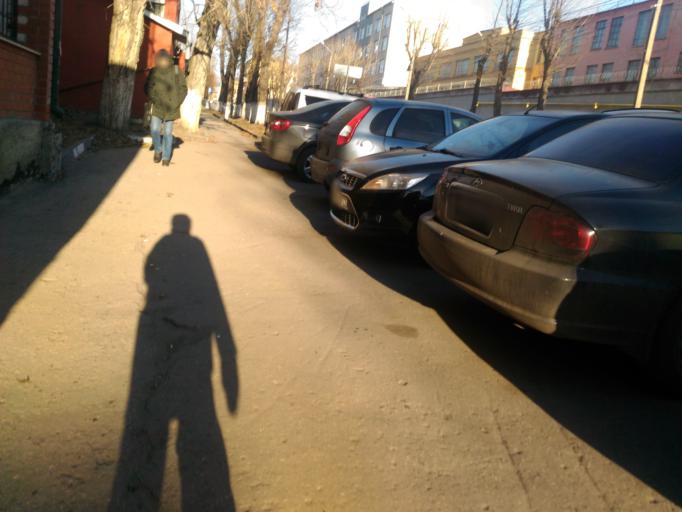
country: RU
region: Ulyanovsk
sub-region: Ulyanovskiy Rayon
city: Ulyanovsk
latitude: 54.3196
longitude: 48.3854
